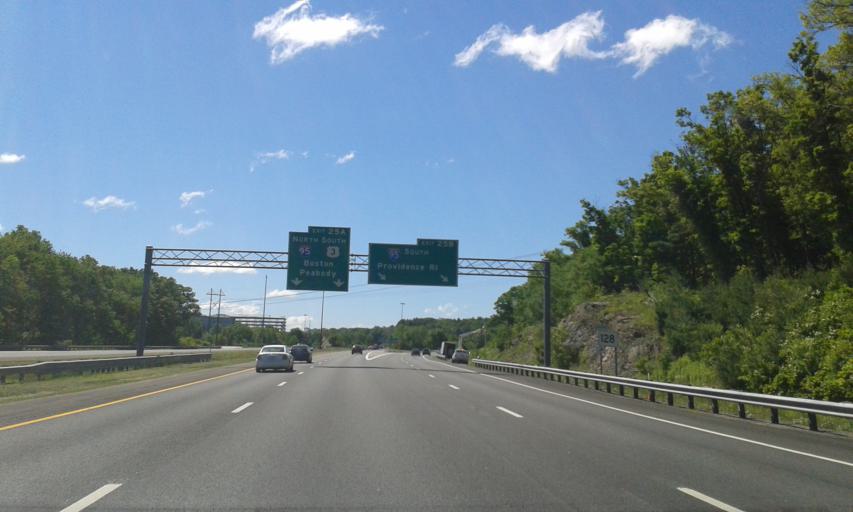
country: US
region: Massachusetts
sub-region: Middlesex County
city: Lexington
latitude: 42.4817
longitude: -71.2236
